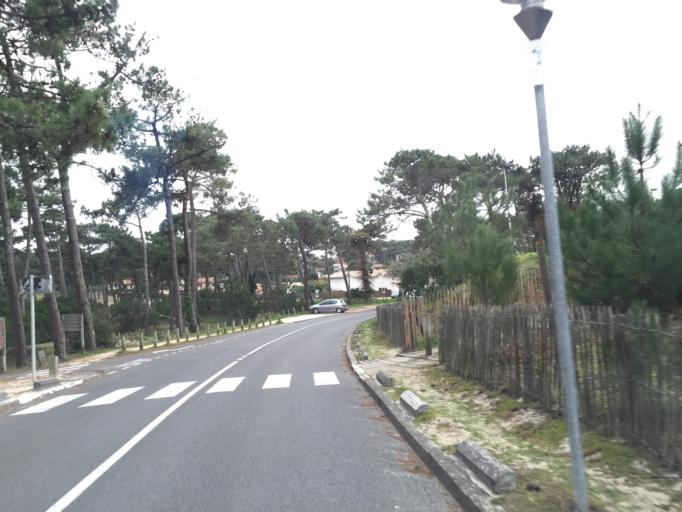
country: FR
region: Aquitaine
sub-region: Departement de la Gironde
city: Lacanau
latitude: 45.0090
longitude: -1.1954
